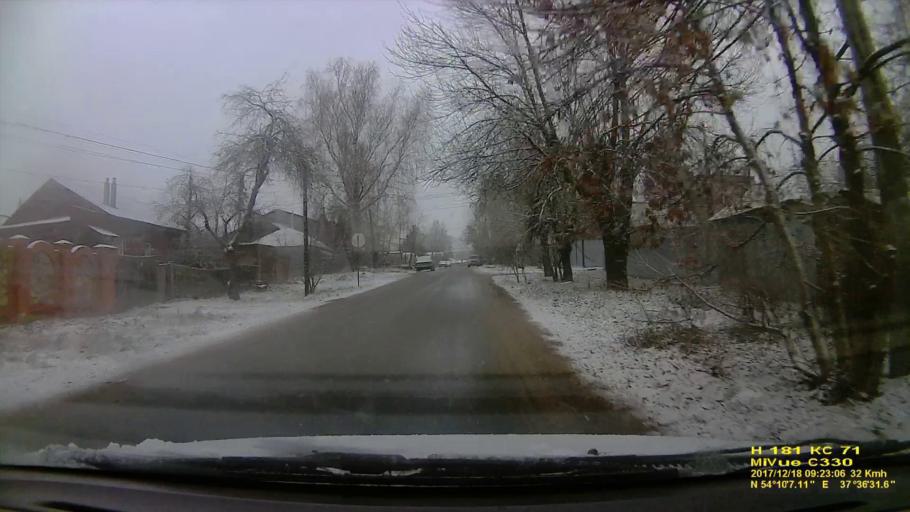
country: RU
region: Tula
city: Tula
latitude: 54.1685
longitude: 37.6087
